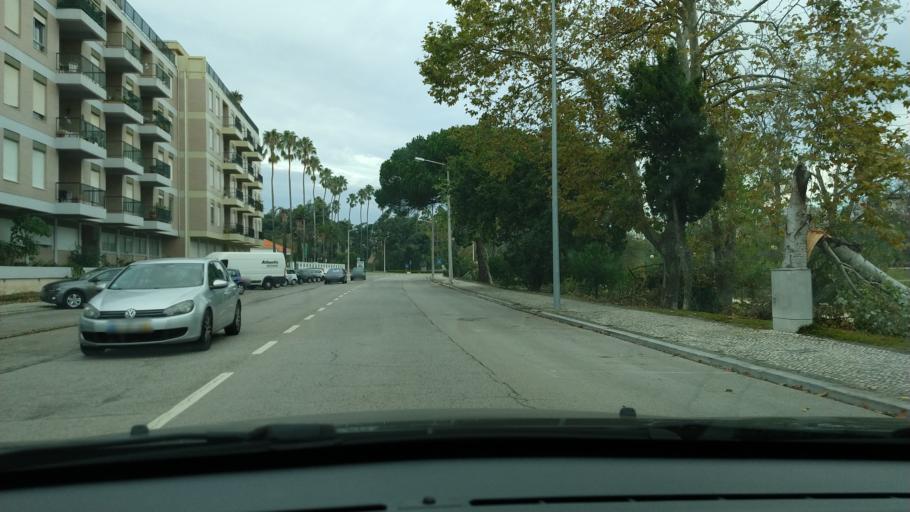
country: PT
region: Coimbra
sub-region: Figueira da Foz
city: Figueira da Foz
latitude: 40.1541
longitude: -8.8621
